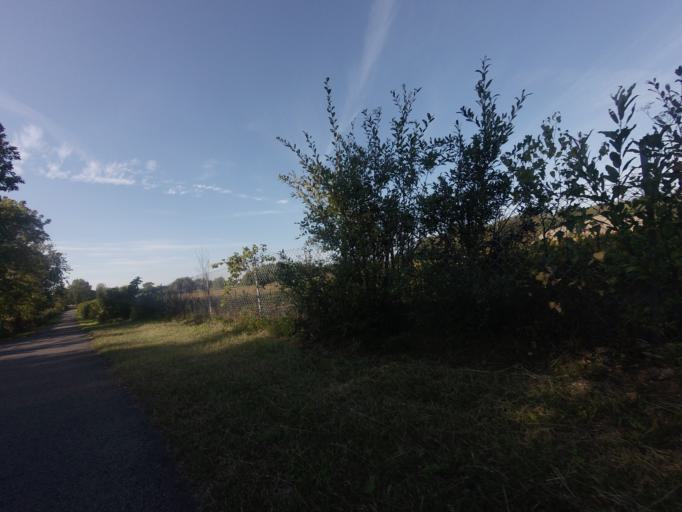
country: CA
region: Quebec
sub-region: Laurentides
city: Saint-Jerome
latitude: 45.7386
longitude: -73.9542
